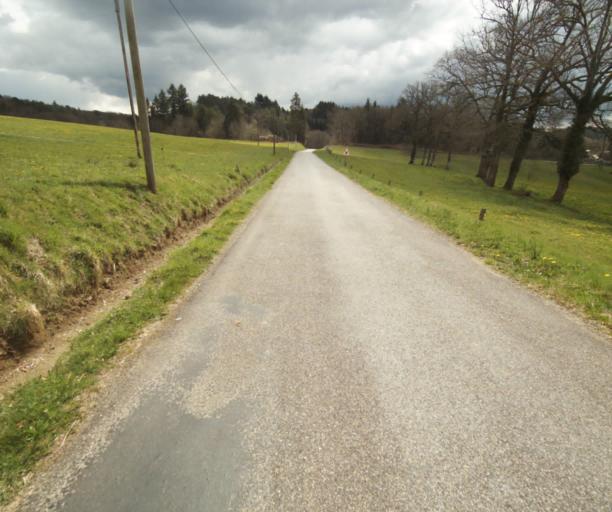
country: FR
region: Limousin
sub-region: Departement de la Correze
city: Laguenne
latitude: 45.2356
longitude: 1.8959
